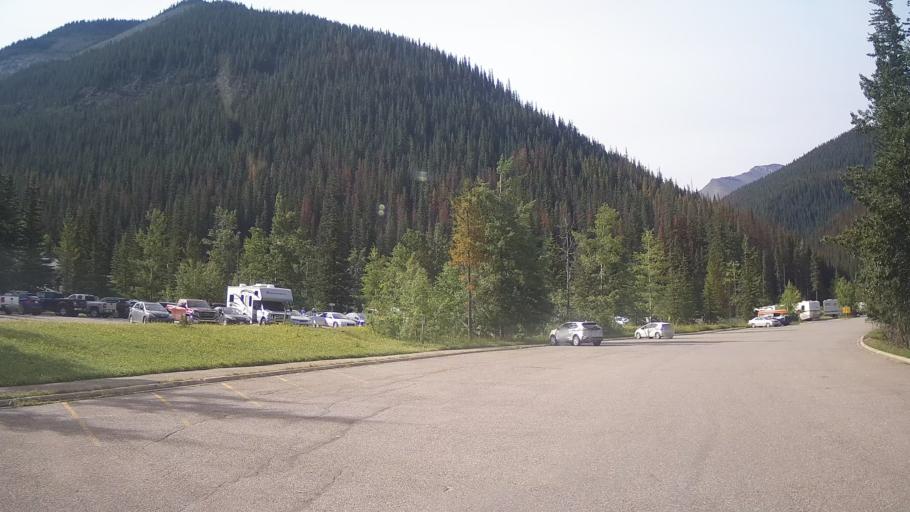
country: CA
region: Alberta
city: Hinton
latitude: 53.1311
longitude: -117.7716
